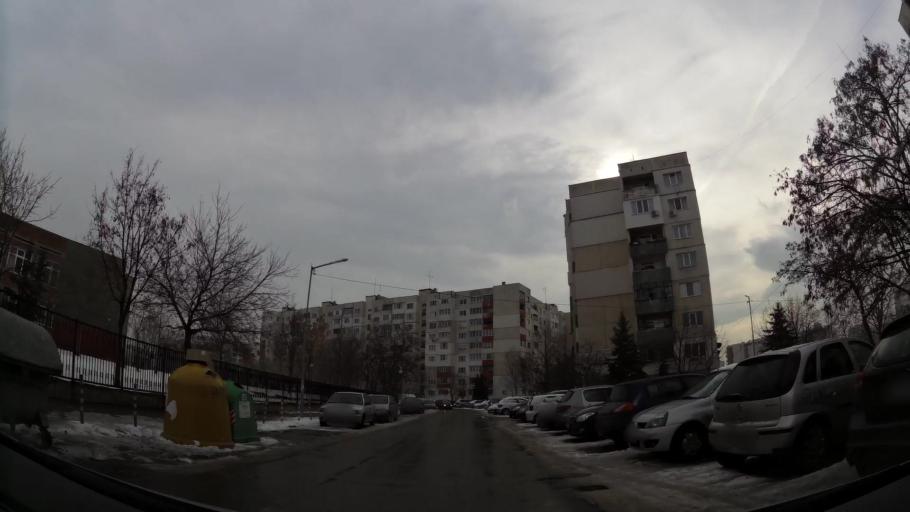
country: BG
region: Sofia-Capital
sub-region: Stolichna Obshtina
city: Sofia
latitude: 42.7134
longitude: 23.3775
